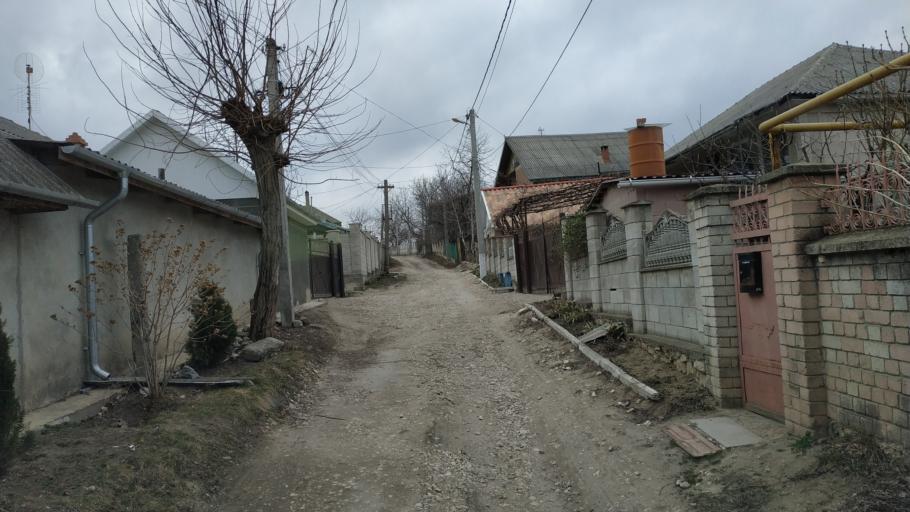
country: MD
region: Laloveni
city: Ialoveni
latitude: 46.9322
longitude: 28.7734
